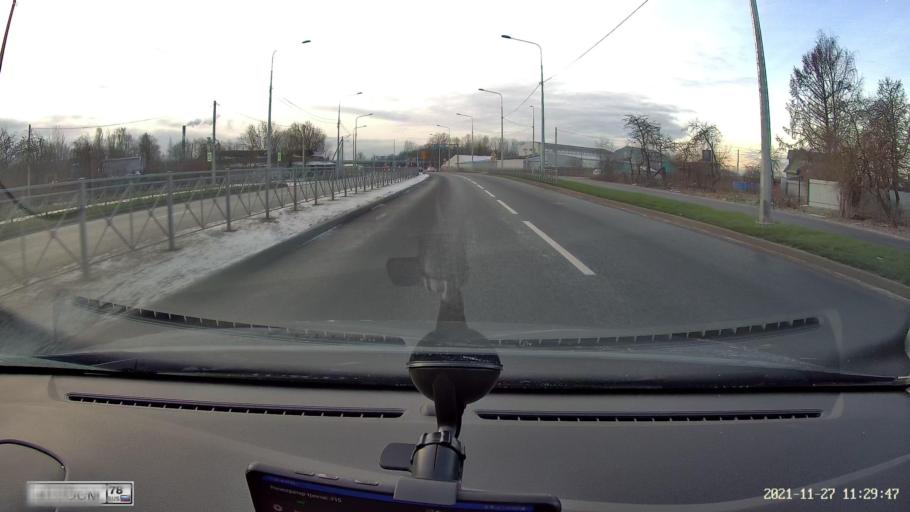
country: RU
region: St.-Petersburg
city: Krasnoye Selo
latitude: 59.7322
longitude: 30.0589
